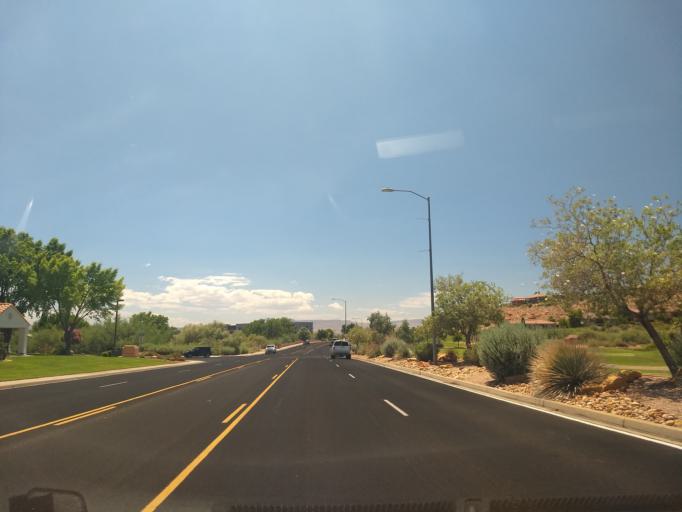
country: US
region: Utah
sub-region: Washington County
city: Washington
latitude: 37.1366
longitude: -113.5263
